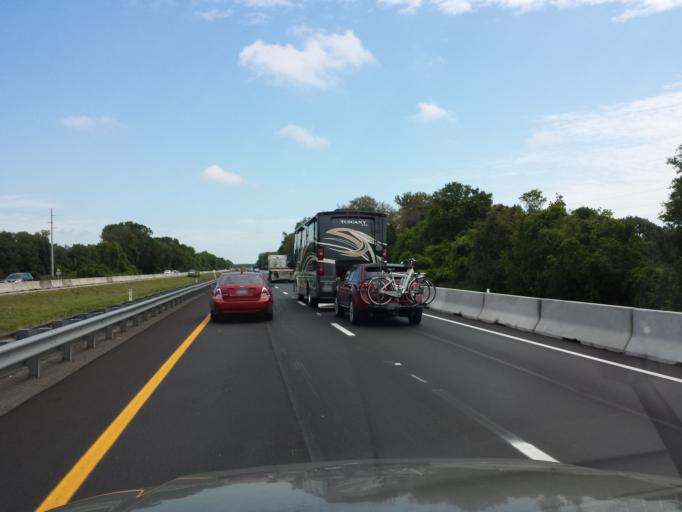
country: US
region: Florida
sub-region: Sumter County
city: Bushnell
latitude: 28.6968
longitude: -82.1273
